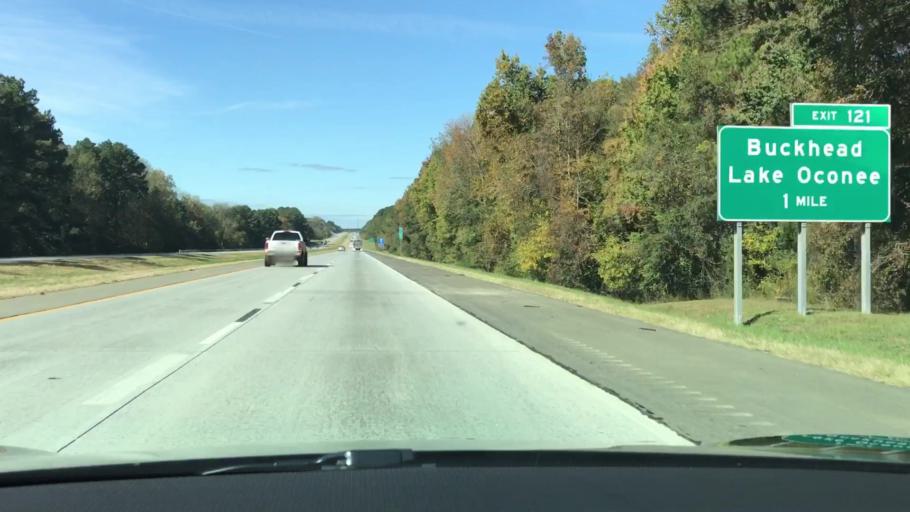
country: US
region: Georgia
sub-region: Putnam County
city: Jefferson
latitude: 33.5455
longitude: -83.3353
